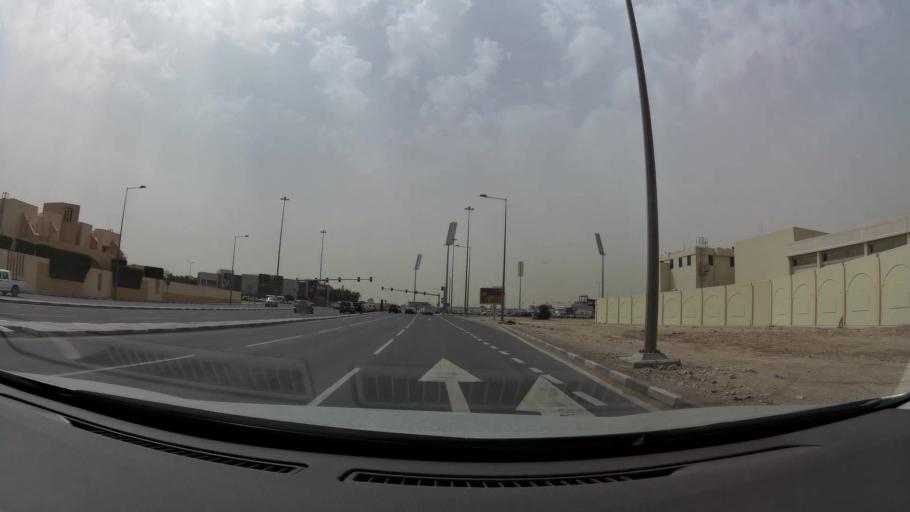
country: QA
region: Baladiyat ad Dawhah
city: Doha
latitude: 25.2556
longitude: 51.5363
